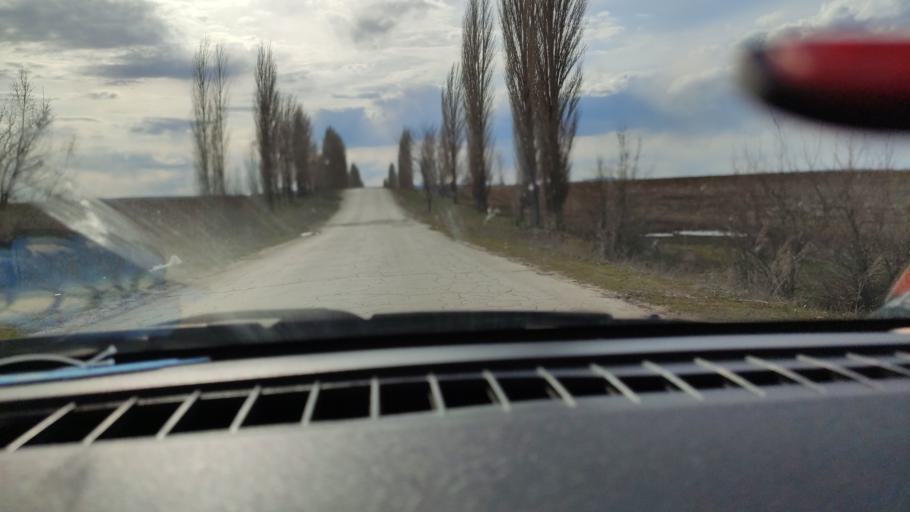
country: RU
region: Saratov
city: Rovnoye
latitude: 50.9384
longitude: 46.1026
